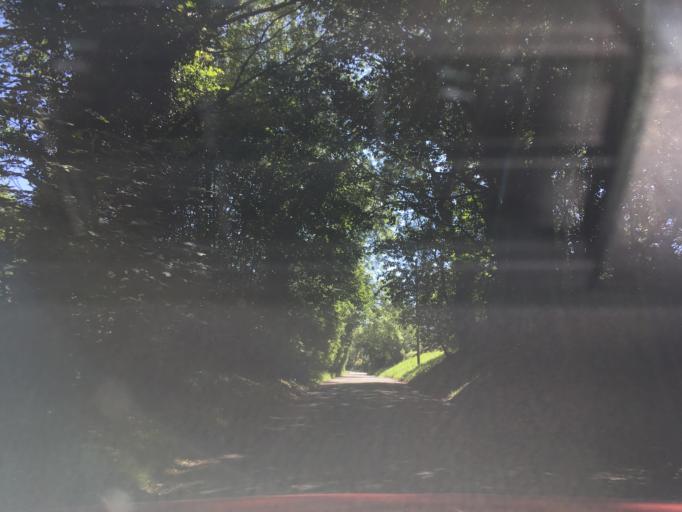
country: GB
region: England
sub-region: Milton Keynes
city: Calverton
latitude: 52.0011
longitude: -0.8308
